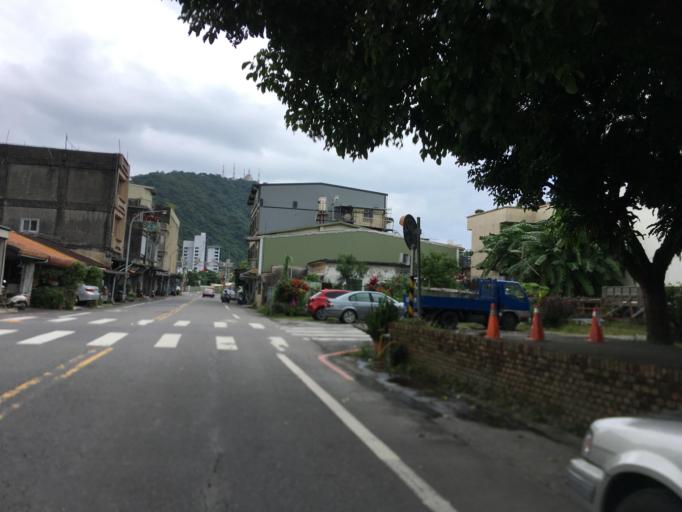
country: TW
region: Taiwan
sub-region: Yilan
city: Yilan
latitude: 24.5926
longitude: 121.8531
